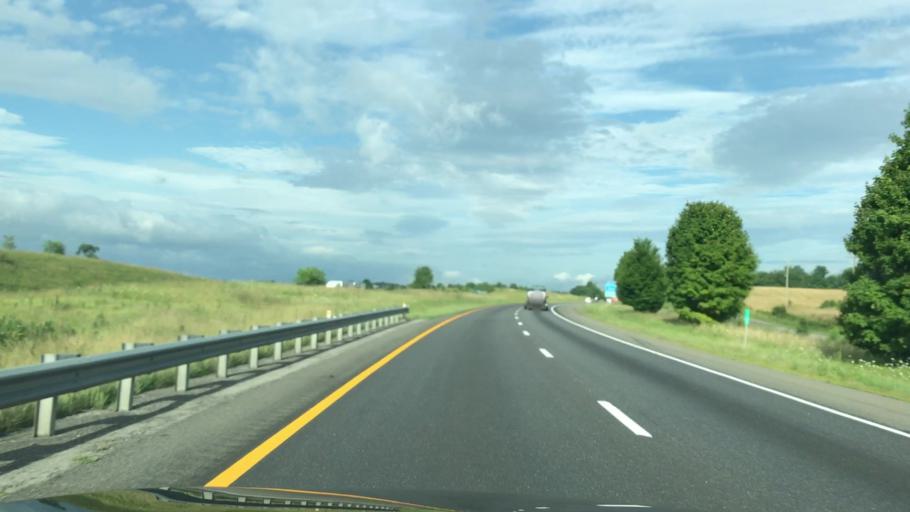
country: US
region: Virginia
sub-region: Montgomery County
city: Christiansburg
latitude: 37.0954
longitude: -80.4806
